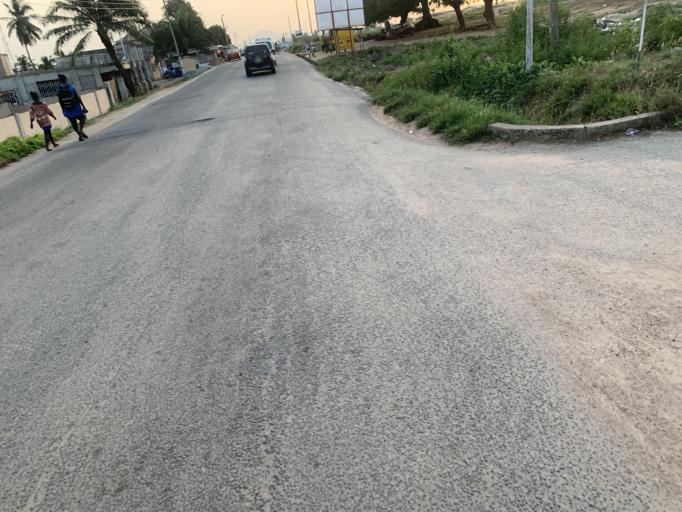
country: GH
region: Central
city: Winneba
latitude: 5.3525
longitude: -0.6185
